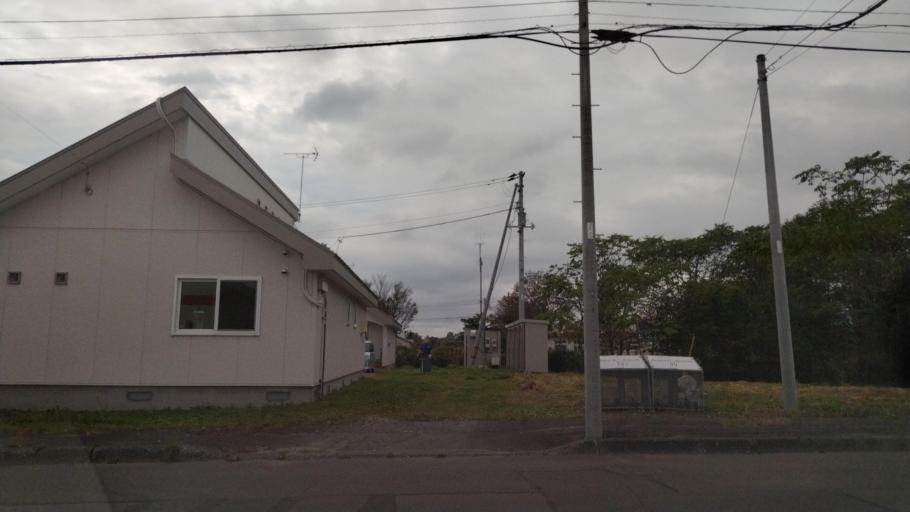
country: JP
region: Hokkaido
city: Otofuke
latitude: 43.2333
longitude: 143.2892
